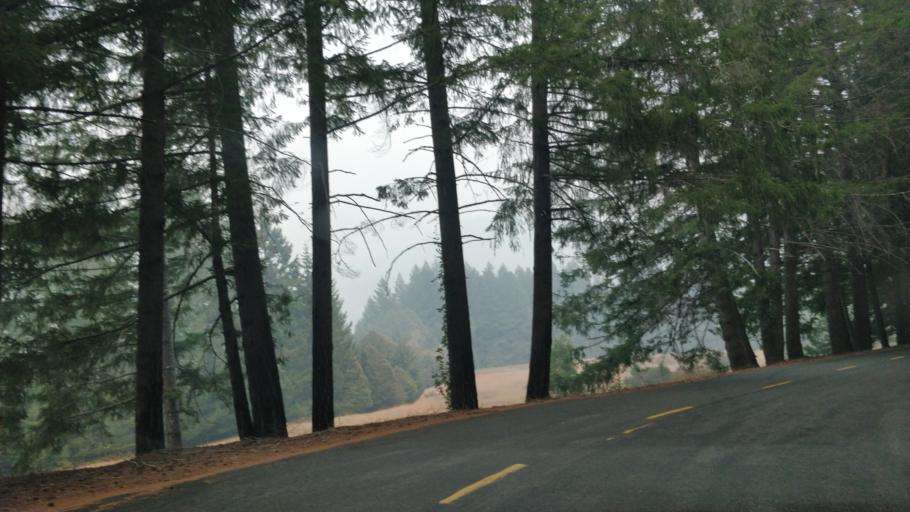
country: US
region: California
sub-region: Humboldt County
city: Rio Dell
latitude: 40.3327
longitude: -124.0362
